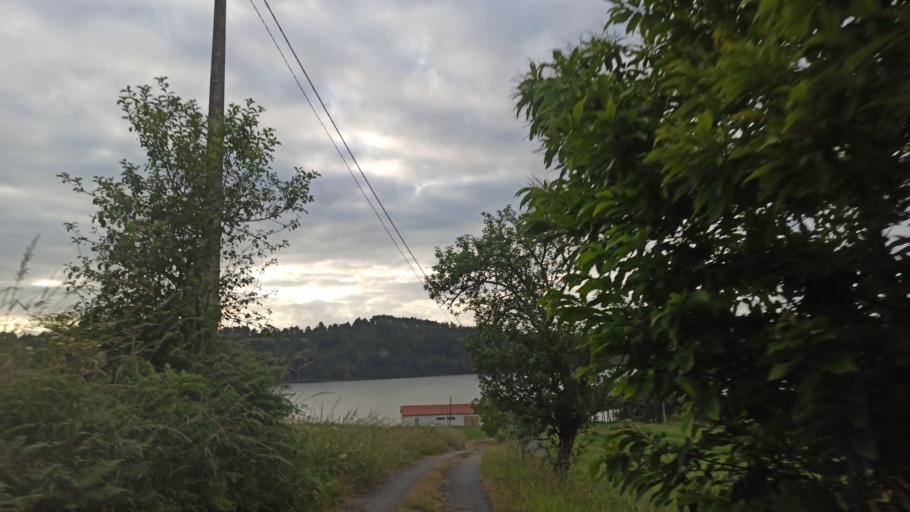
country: ES
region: Galicia
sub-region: Provincia da Coruna
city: Santiso
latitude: 42.8344
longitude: -8.1230
